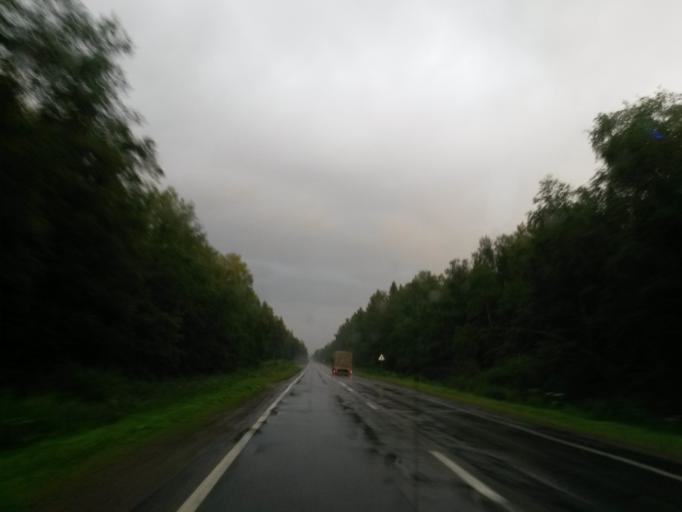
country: RU
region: Jaroslavl
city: Gavrilov-Yam
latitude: 57.4327
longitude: 39.9181
